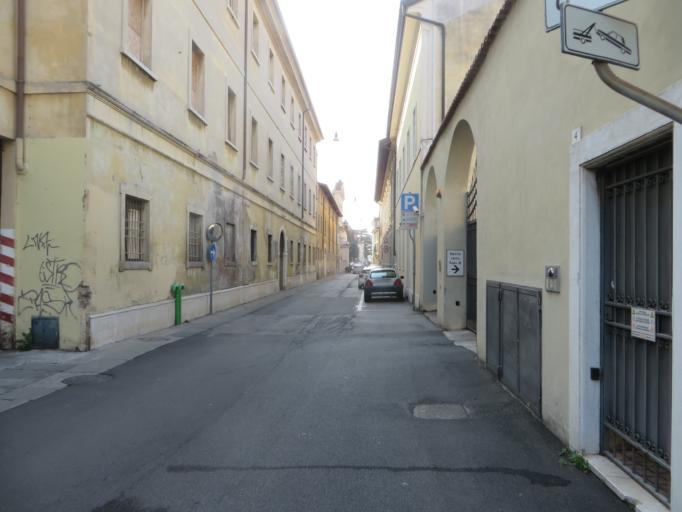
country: IT
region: Lombardy
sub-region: Provincia di Brescia
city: Brescia
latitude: 45.5342
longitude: 10.2287
